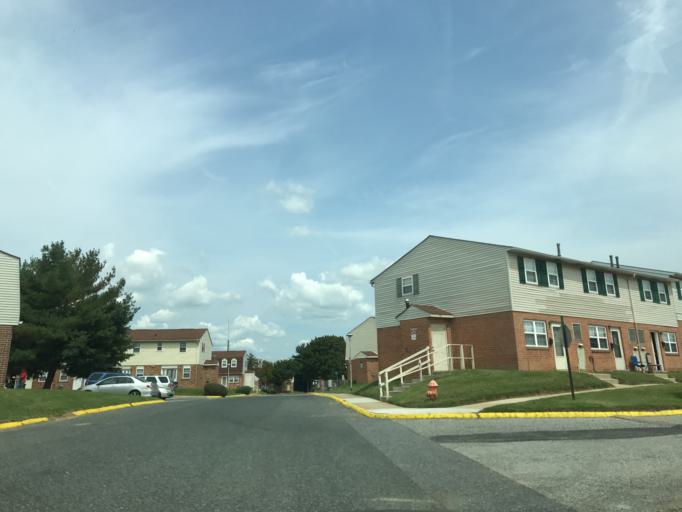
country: US
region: Maryland
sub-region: Baltimore County
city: Middle River
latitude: 39.3057
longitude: -76.4458
